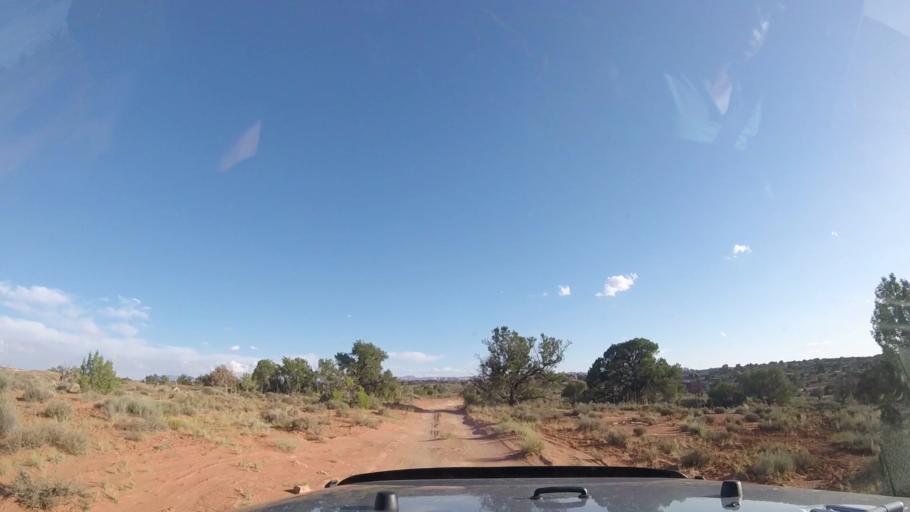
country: US
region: Utah
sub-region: Grand County
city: Moab
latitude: 38.2103
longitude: -109.7876
